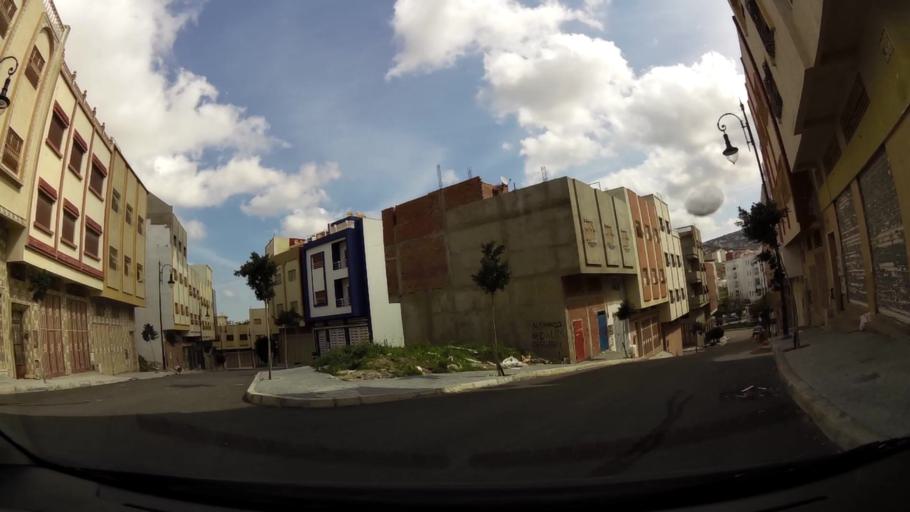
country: MA
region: Tanger-Tetouan
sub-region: Tanger-Assilah
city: Tangier
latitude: 35.7676
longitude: -5.7624
